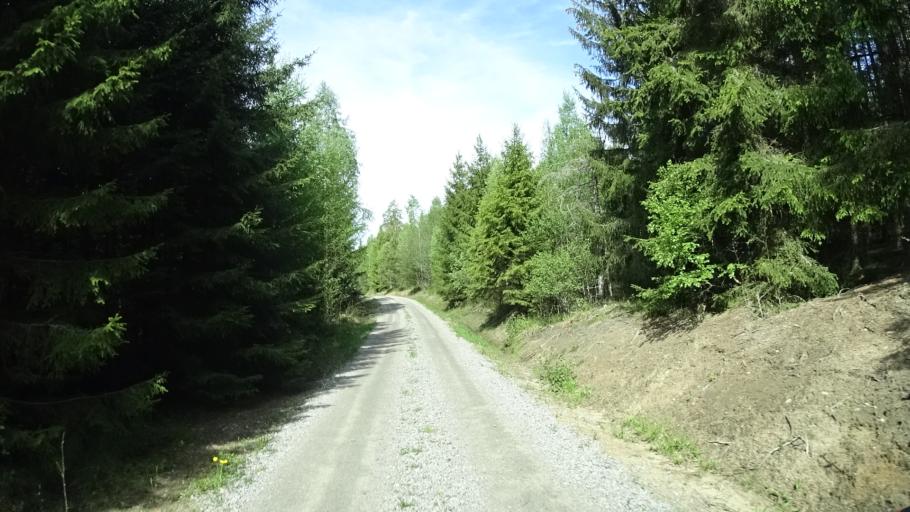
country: SE
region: OEstergoetland
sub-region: Finspangs Kommun
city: Finspang
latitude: 58.7939
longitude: 15.8591
